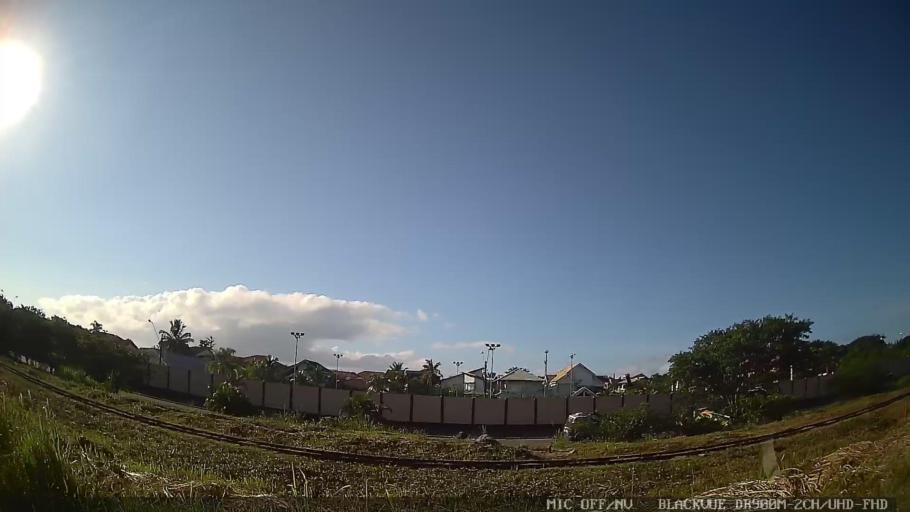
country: BR
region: Sao Paulo
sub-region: Peruibe
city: Peruibe
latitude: -24.2802
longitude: -46.9592
